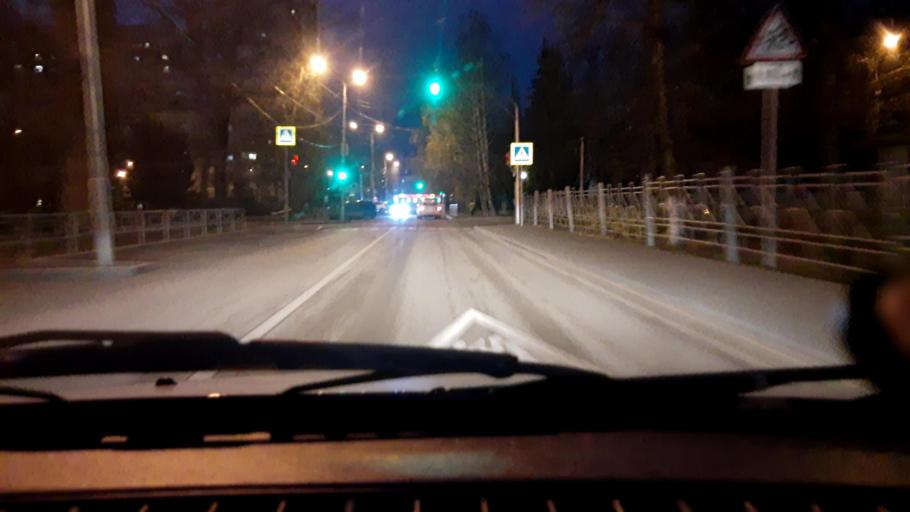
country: RU
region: Bashkortostan
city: Ufa
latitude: 54.7204
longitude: 56.0144
